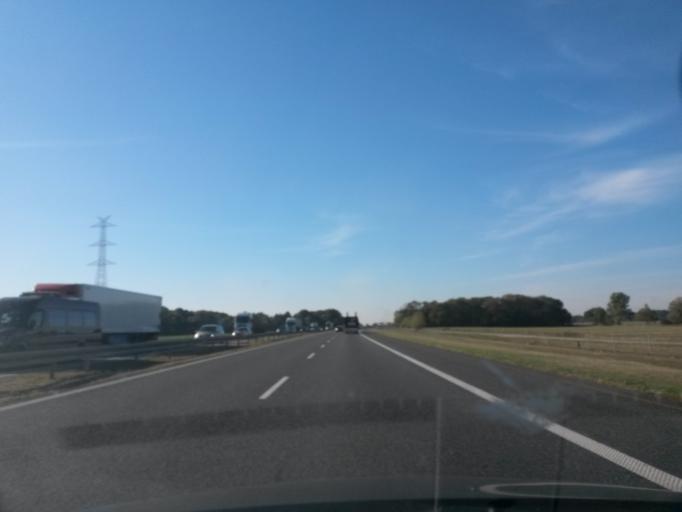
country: PL
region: Opole Voivodeship
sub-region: Powiat brzeski
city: Grodkow
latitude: 50.7721
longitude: 17.3741
